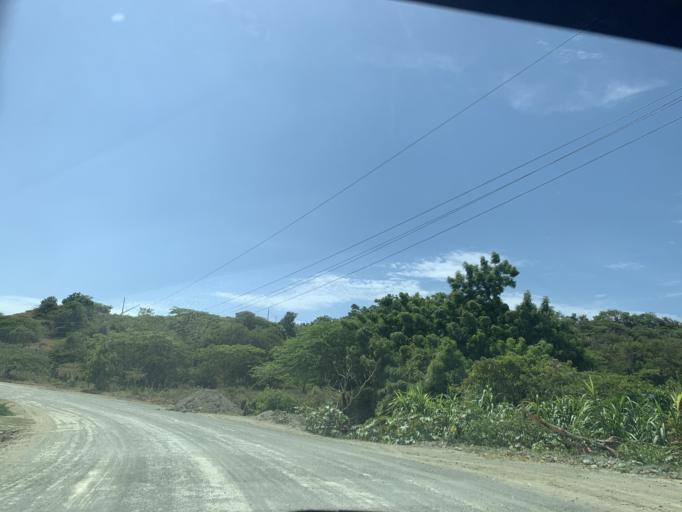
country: DO
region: Puerto Plata
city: Imbert
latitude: 19.8680
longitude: -70.8195
